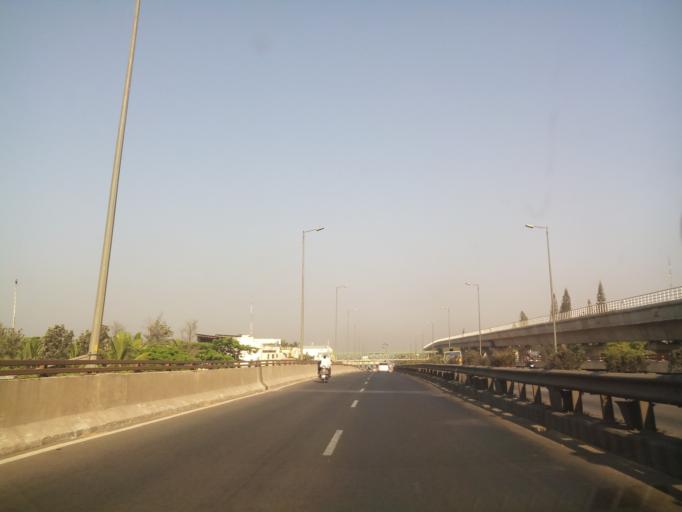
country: IN
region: Karnataka
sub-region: Bangalore Urban
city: Yelahanka
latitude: 13.0479
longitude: 77.4997
